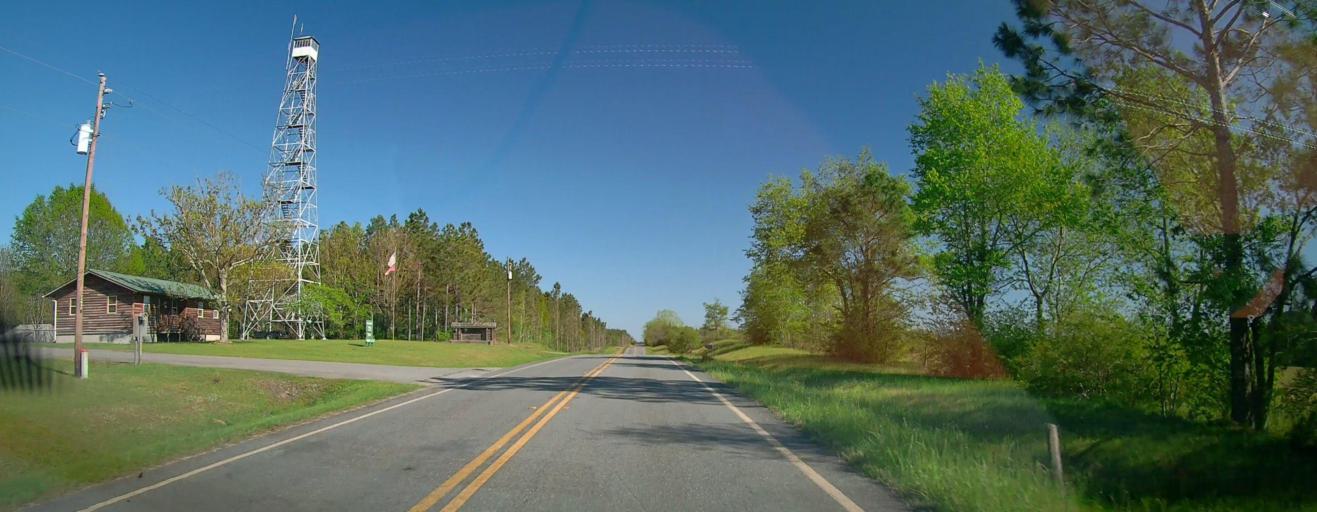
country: US
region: Georgia
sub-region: Wilcox County
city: Rochelle
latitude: 32.0020
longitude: -83.4813
